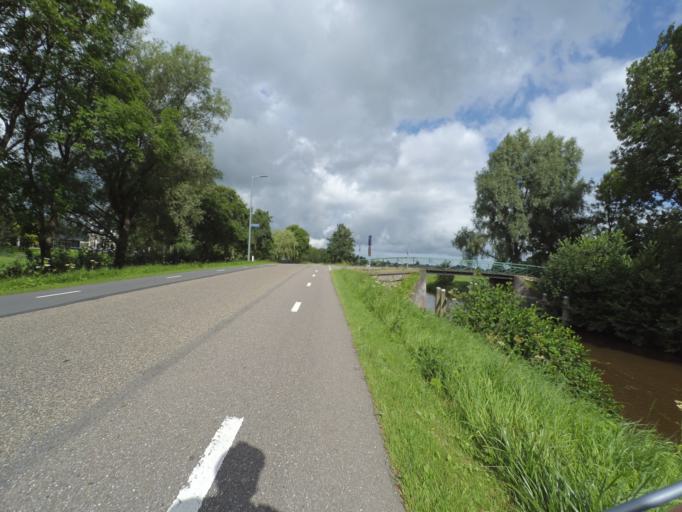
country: NL
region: Friesland
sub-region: Gemeente Kollumerland en Nieuwkruisland
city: Kollum
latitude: 53.2660
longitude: 6.1638
